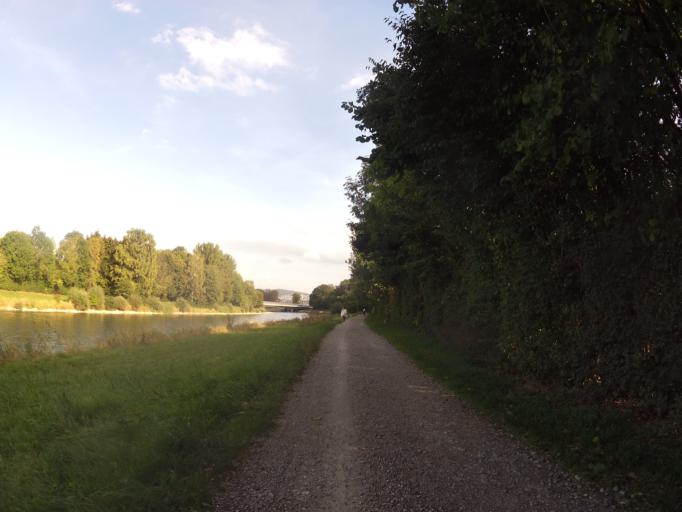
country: CH
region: Zurich
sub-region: Bezirk Dietikon
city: Oberengstringen / Zentrum
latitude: 47.4039
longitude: 8.4626
